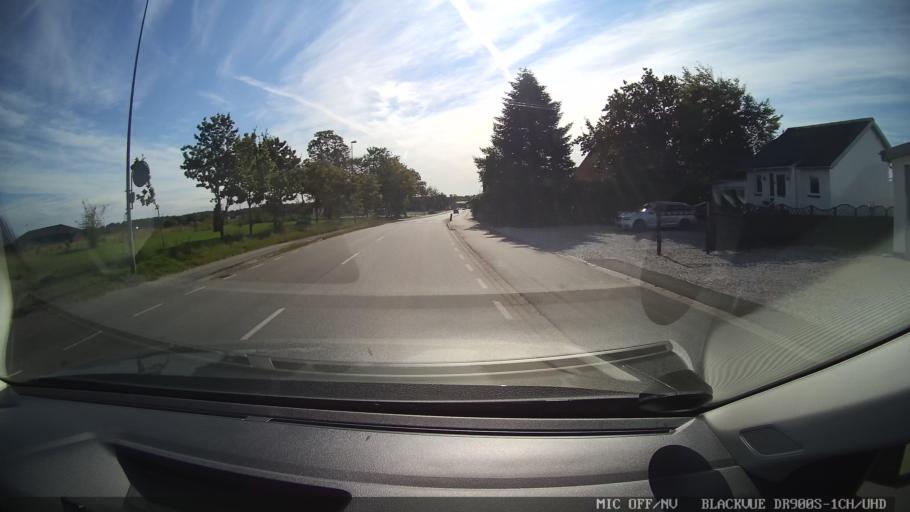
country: DK
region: North Denmark
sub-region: Mariagerfjord Kommune
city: Arden
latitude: 56.7714
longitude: 9.8509
